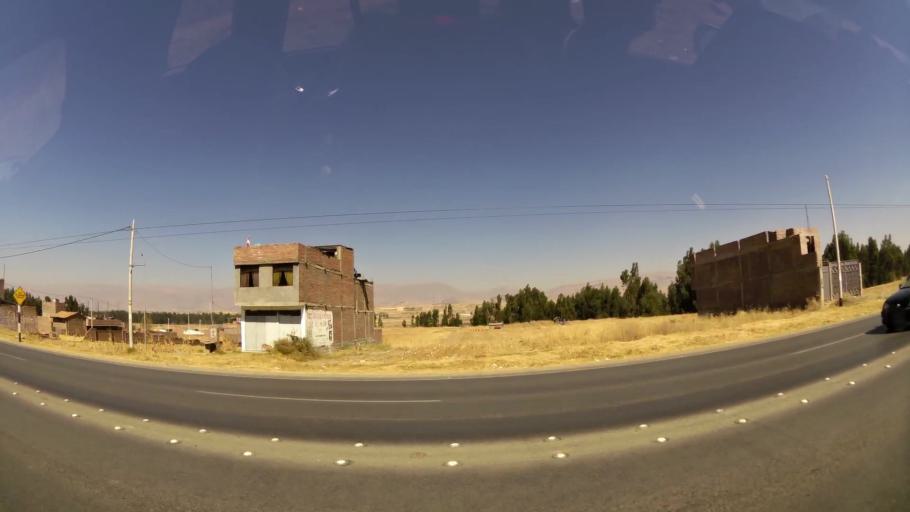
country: PE
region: Junin
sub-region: Provincia de Huancayo
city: San Agustin
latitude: -11.9744
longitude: -75.2668
